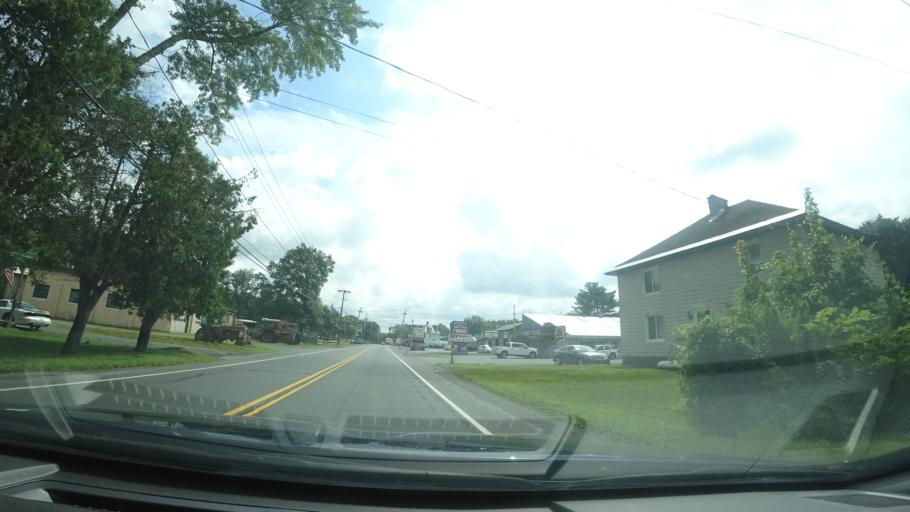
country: US
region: New York
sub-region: Washington County
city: Hudson Falls
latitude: 43.3197
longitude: -73.5890
